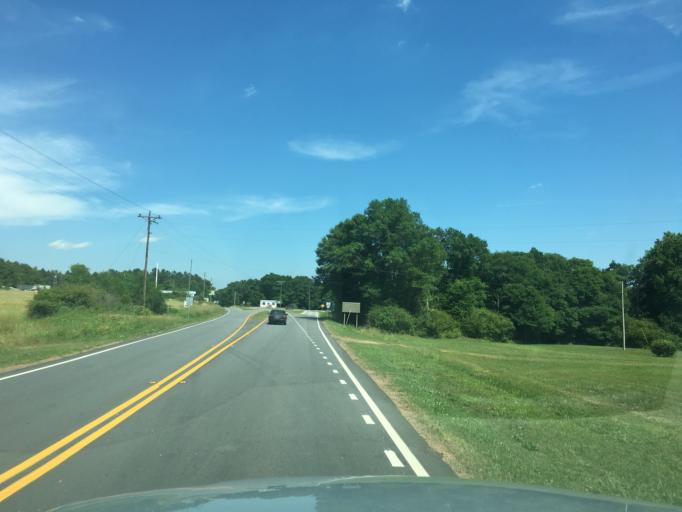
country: US
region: Georgia
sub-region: Hart County
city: Reed Creek
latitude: 34.5093
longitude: -82.9700
